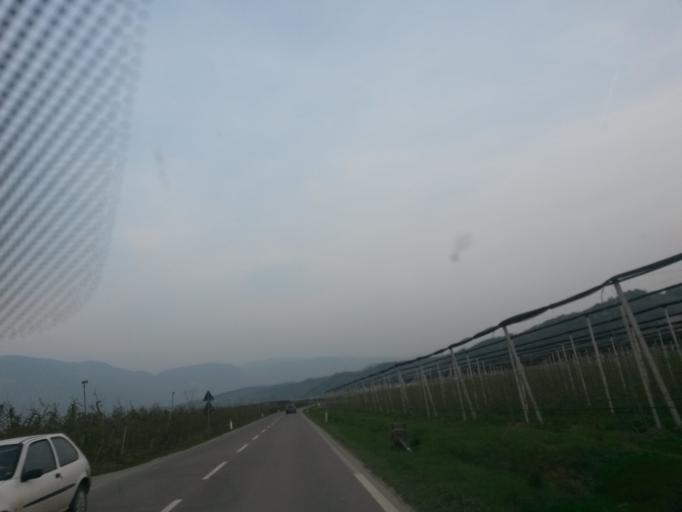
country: IT
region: Trentino-Alto Adige
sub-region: Bolzano
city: Andriano
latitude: 46.5033
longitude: 11.2508
